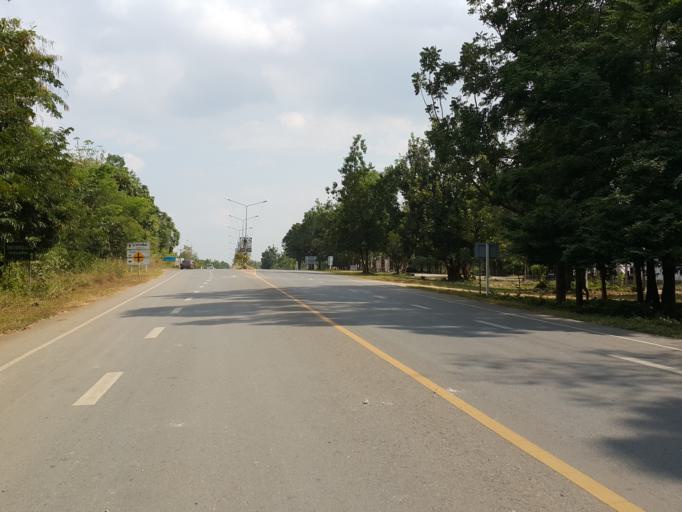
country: TH
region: Sukhothai
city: Thung Saliam
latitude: 17.3320
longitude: 99.5348
